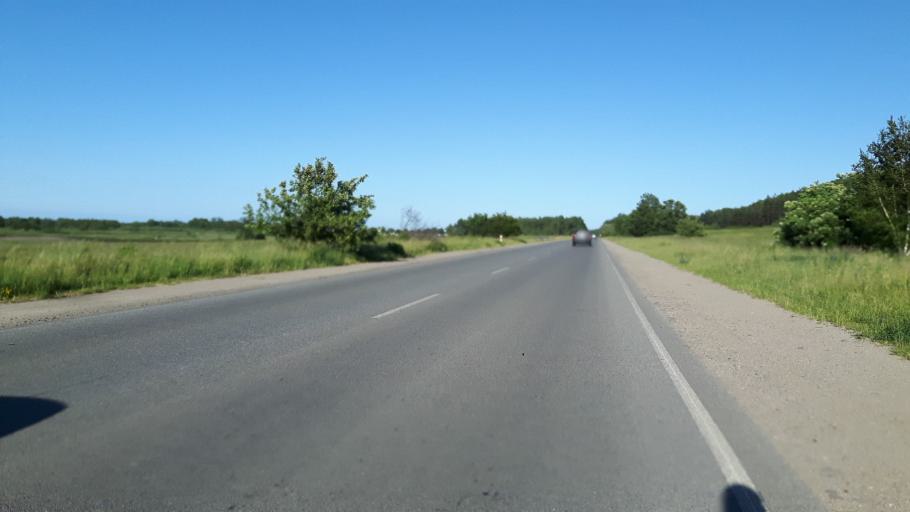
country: PL
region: Pomeranian Voivodeship
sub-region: Powiat pucki
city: Kosakowo
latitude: 54.6050
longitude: 18.4404
